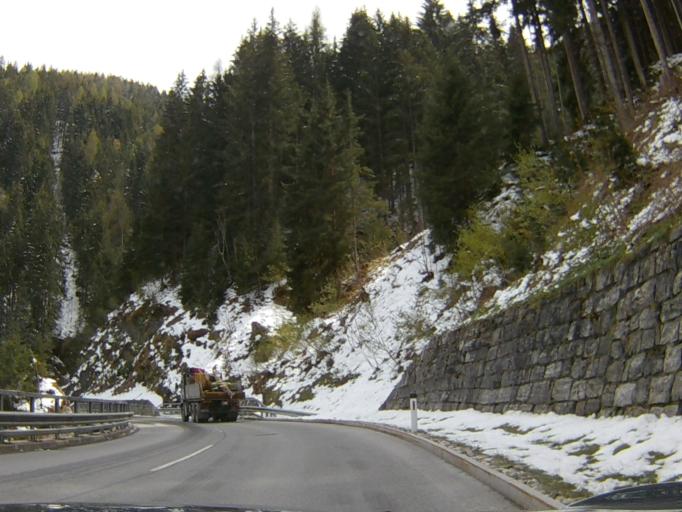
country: AT
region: Tyrol
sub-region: Politischer Bezirk Schwaz
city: Gerlosberg
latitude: 47.2112
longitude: 11.9389
